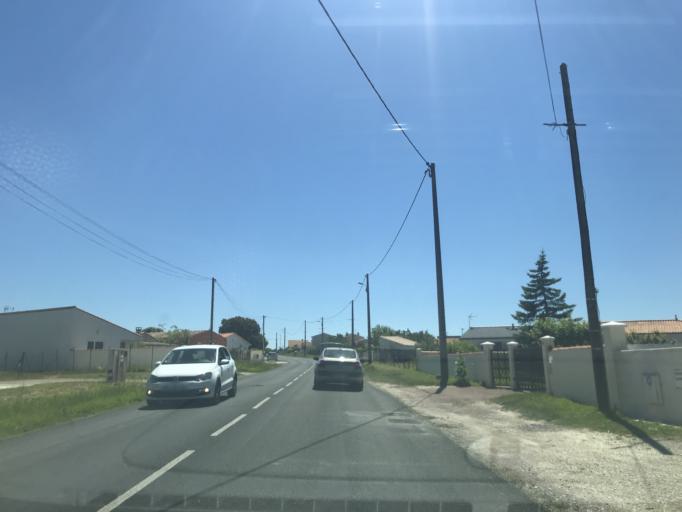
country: FR
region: Poitou-Charentes
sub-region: Departement de la Charente-Maritime
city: Meschers-sur-Gironde
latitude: 45.5776
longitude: -0.9601
